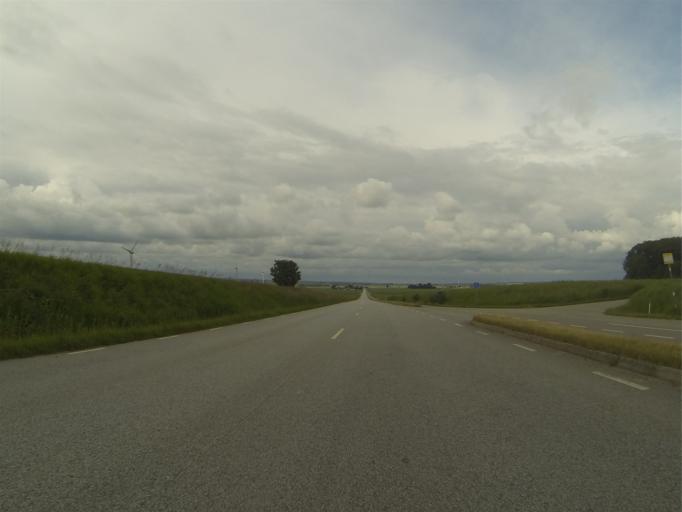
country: SE
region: Skane
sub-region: Eslovs Kommun
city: Eslov
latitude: 55.7469
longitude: 13.2899
